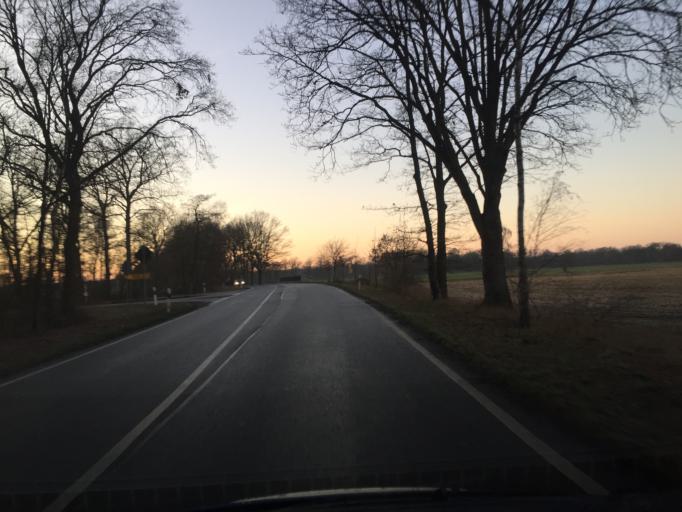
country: DE
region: Lower Saxony
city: Adelheidsdorf
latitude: 52.5228
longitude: 10.0489
